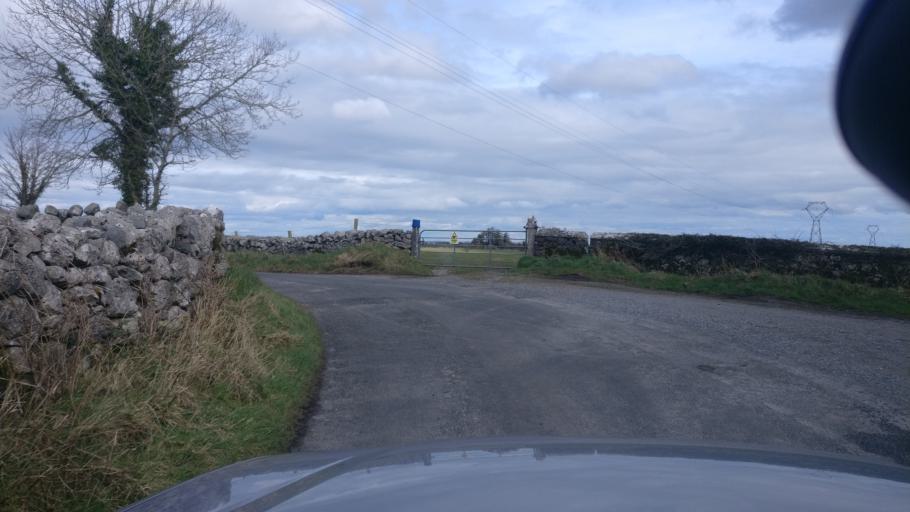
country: IE
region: Connaught
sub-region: County Galway
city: Loughrea
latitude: 53.1891
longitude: -8.4889
